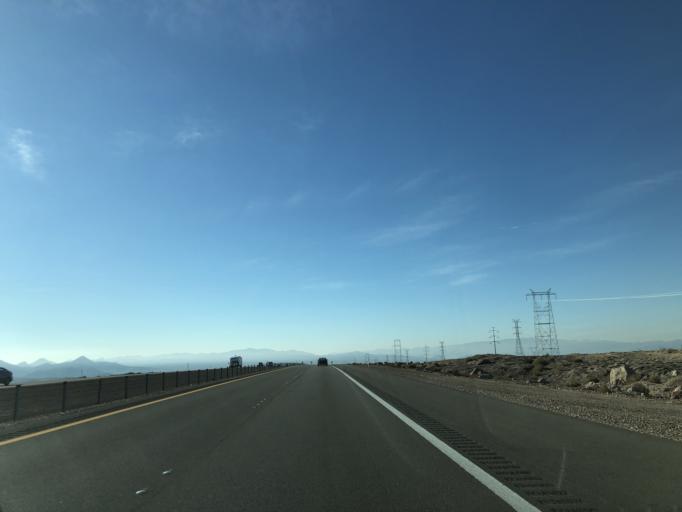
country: US
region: Nevada
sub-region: Clark County
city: Boulder City
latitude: 35.9522
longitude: -114.8049
